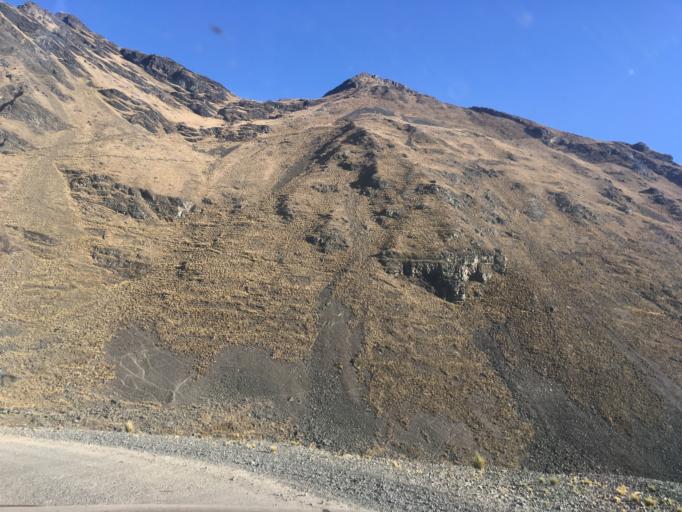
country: BO
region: La Paz
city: Quime
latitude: -17.0236
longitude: -67.2818
